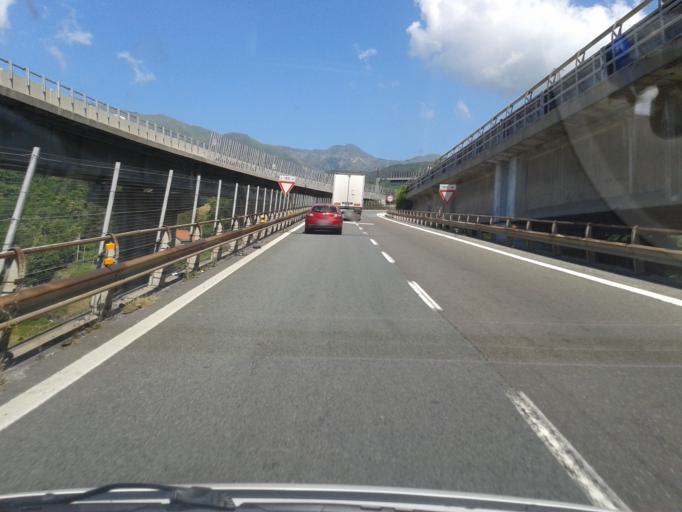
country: IT
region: Liguria
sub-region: Provincia di Genova
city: Mele
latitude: 44.4343
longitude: 8.7395
